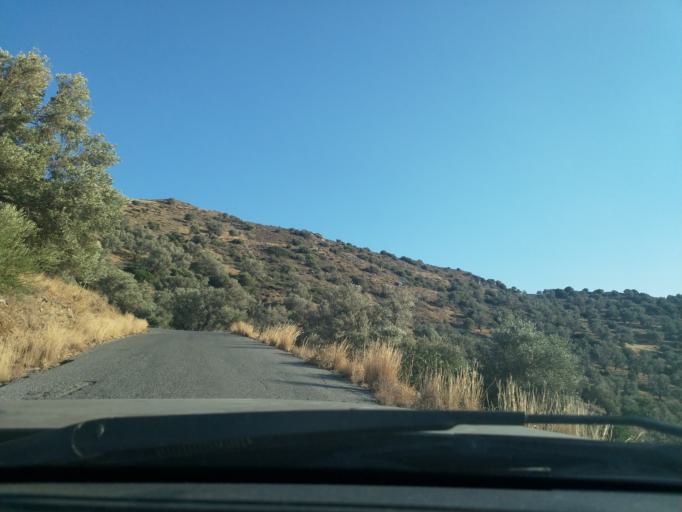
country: GR
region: Crete
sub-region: Nomos Rethymnis
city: Agia Galini
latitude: 35.1116
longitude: 24.5662
